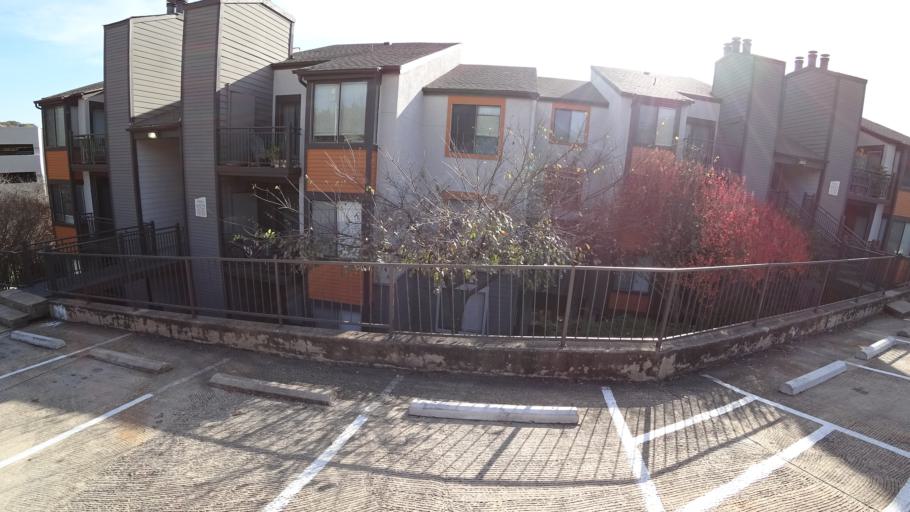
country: US
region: Texas
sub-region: Williamson County
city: Jollyville
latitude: 30.3875
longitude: -97.7617
